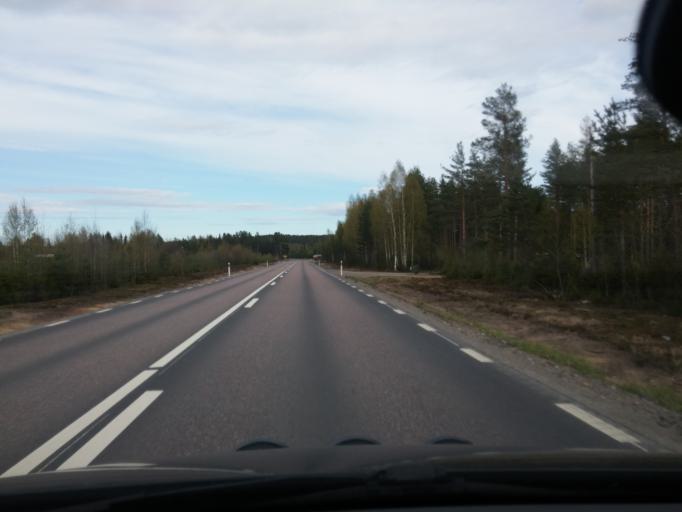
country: SE
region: Gaevleborg
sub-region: Ljusdals Kommun
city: Ljusdal
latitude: 61.8165
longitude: 16.0119
